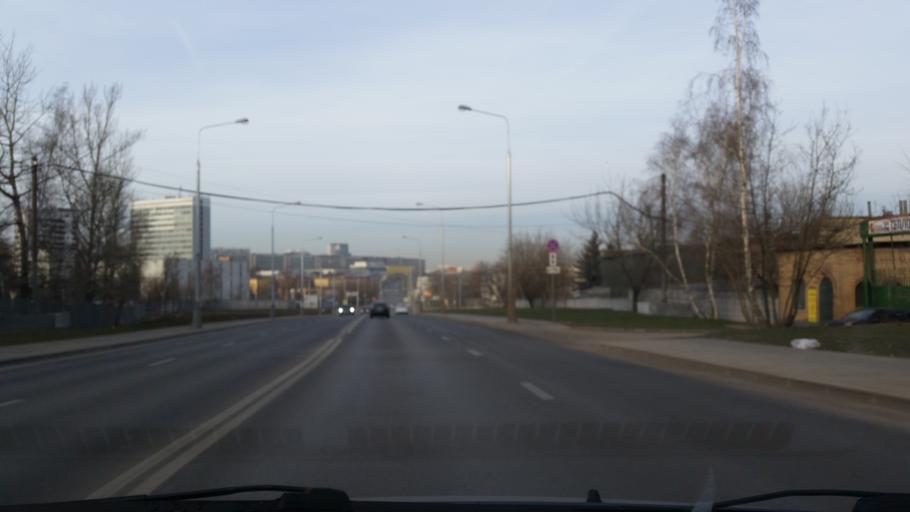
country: RU
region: Moscow
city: Tsaritsyno
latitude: 55.6174
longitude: 37.6263
